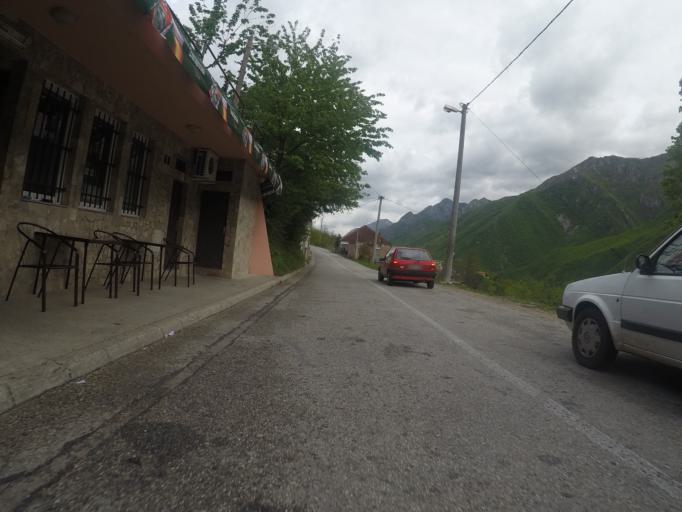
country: BA
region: Federation of Bosnia and Herzegovina
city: Siroki Brijeg
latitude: 43.5416
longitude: 17.5782
